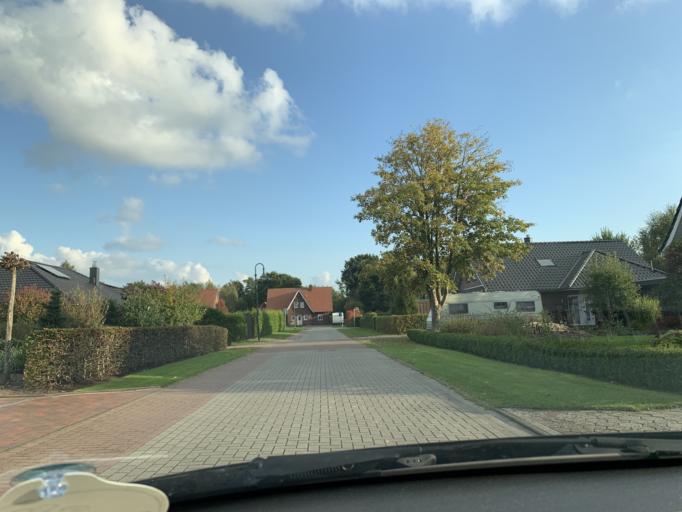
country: DE
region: Lower Saxony
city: Apen
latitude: 53.2421
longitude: 7.7871
